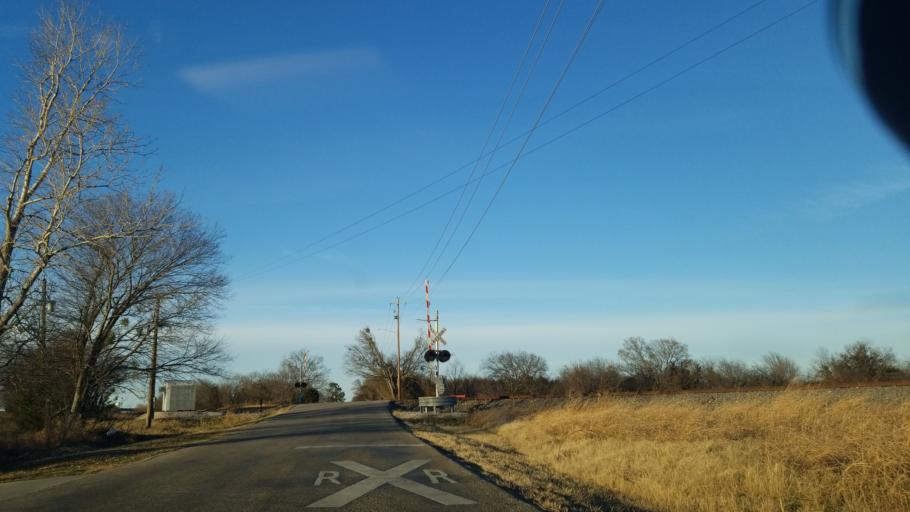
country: US
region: Texas
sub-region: Denton County
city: Denton
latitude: 33.1933
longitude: -97.1616
